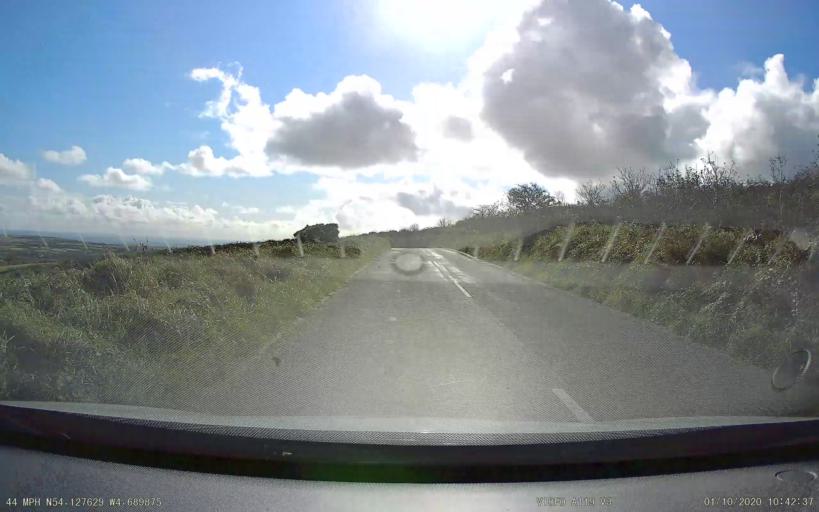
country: IM
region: Castletown
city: Castletown
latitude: 54.1276
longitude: -4.6899
